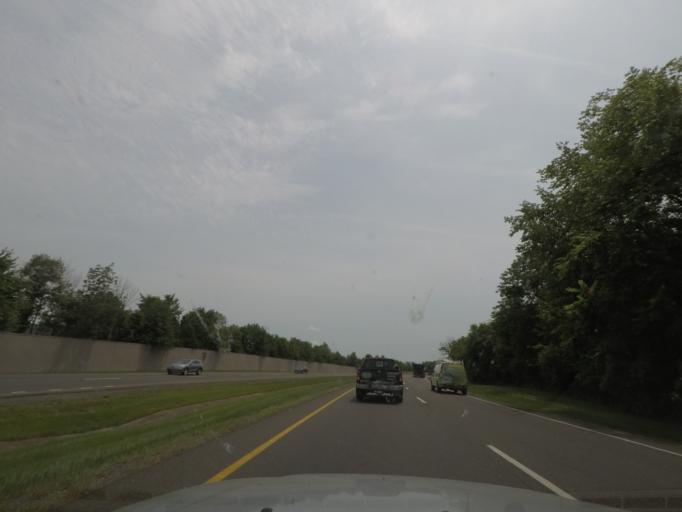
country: US
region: Virginia
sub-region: Prince William County
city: Haymarket
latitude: 38.8346
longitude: -77.6331
